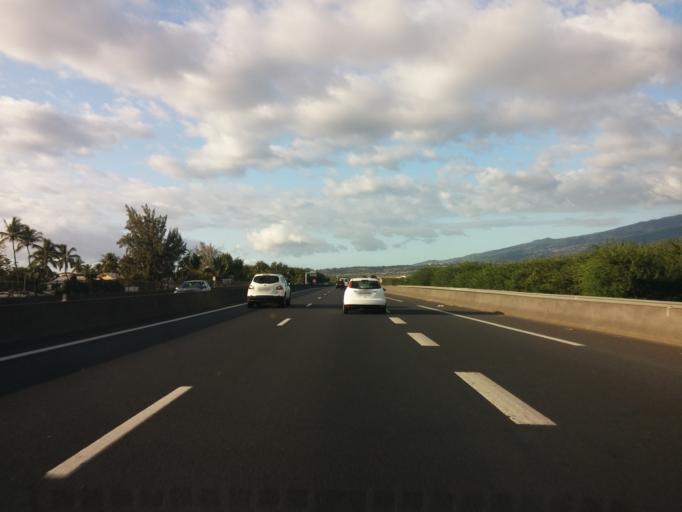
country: RE
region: Reunion
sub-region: Reunion
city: Saint-Paul
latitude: -21.0069
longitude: 55.2793
